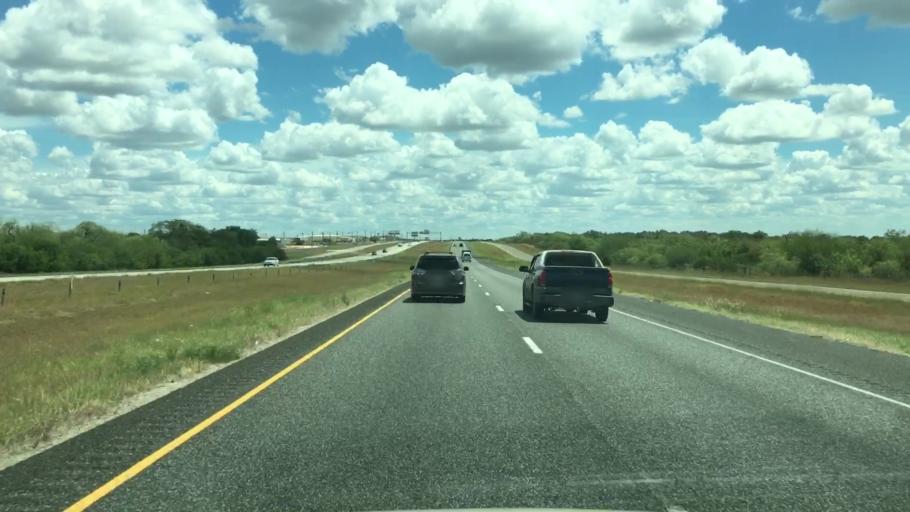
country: US
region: Texas
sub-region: Atascosa County
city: Pleasanton
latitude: 28.8971
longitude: -98.4167
